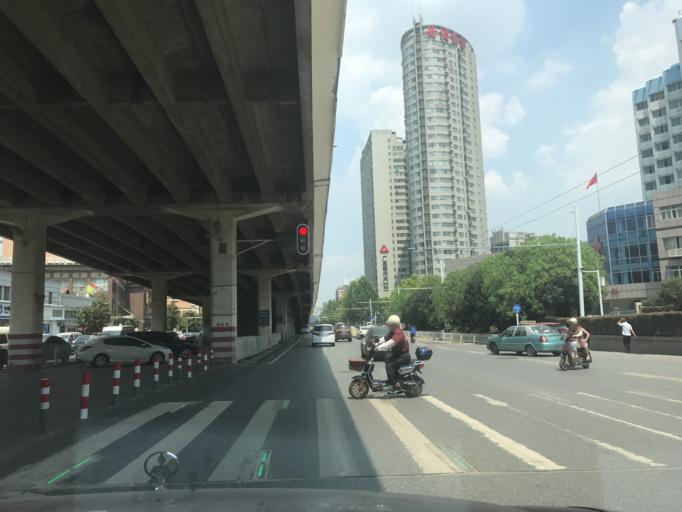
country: CN
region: Hubei
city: Jiang'an
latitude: 30.6166
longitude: 114.3028
